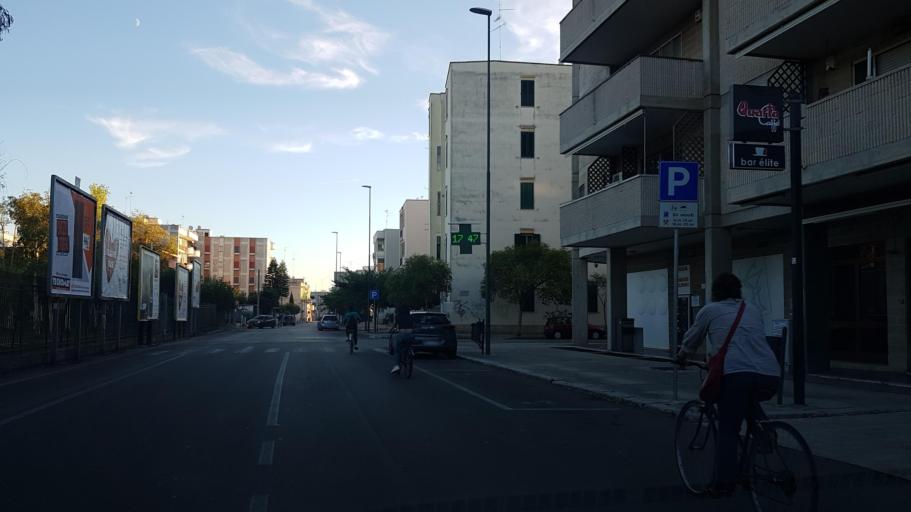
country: IT
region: Apulia
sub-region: Provincia di Lecce
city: Lecce
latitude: 40.3657
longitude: 18.1768
